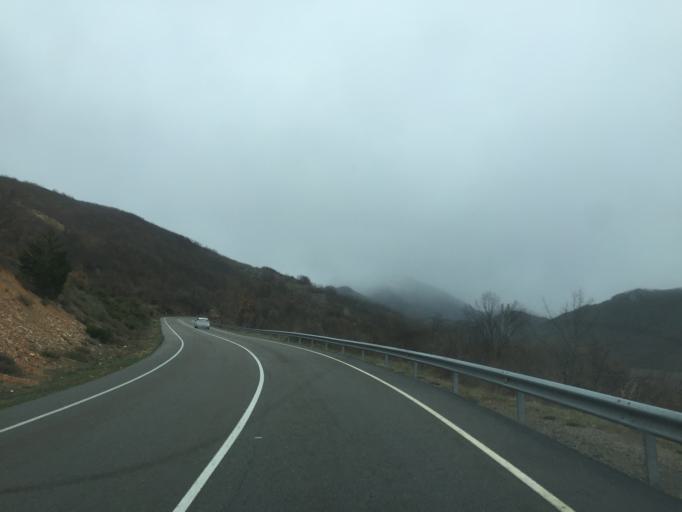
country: ES
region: Castille and Leon
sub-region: Provincia de Leon
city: Sena de Luna
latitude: 42.8993
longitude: -5.9030
